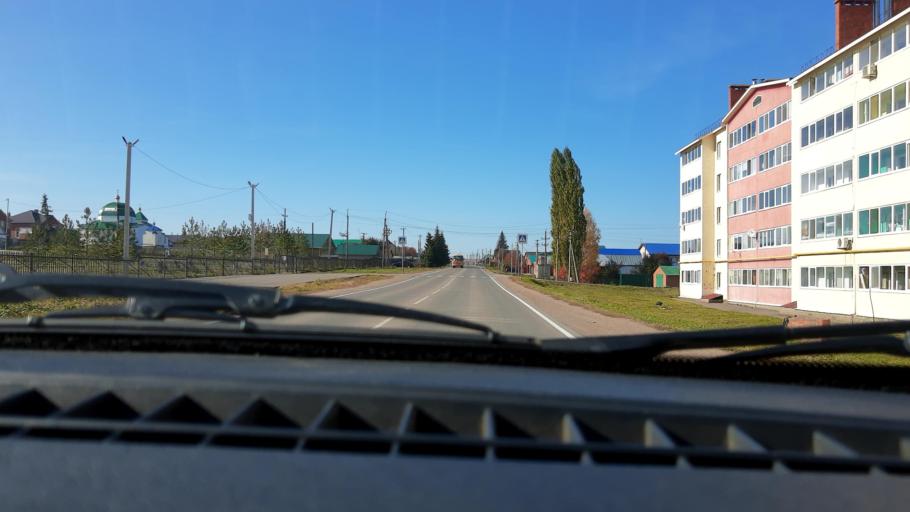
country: RU
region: Bashkortostan
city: Mikhaylovka
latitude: 54.8153
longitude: 55.7960
